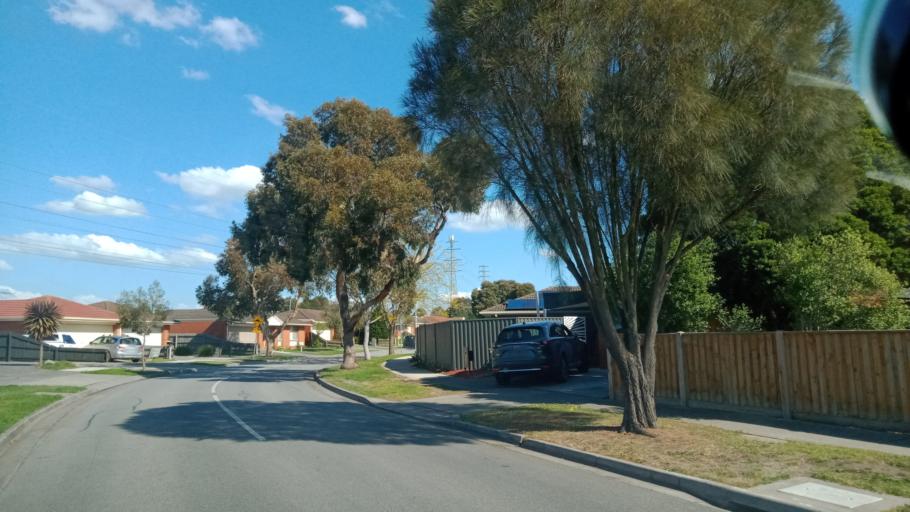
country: AU
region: Victoria
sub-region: Casey
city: Cranbourne West
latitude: -38.1010
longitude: 145.2628
